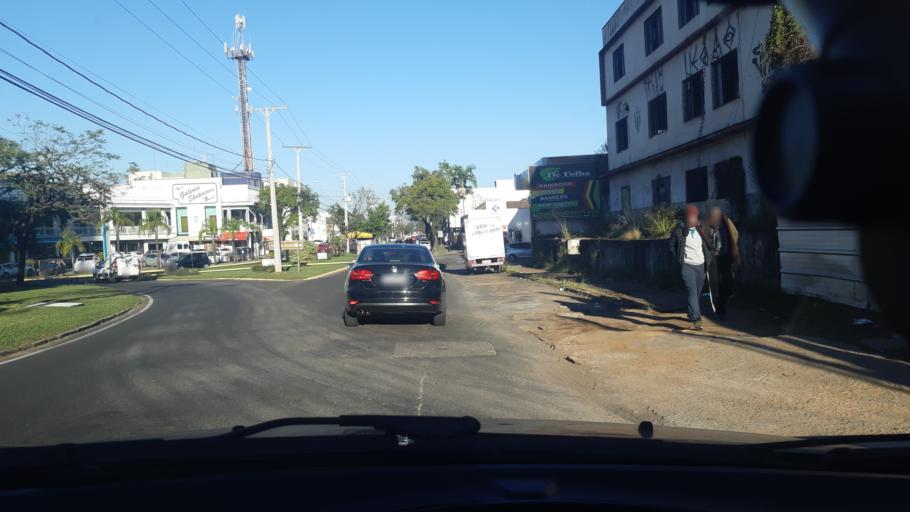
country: BR
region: Rio Grande do Sul
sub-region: Sao Leopoldo
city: Sao Leopoldo
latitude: -29.7701
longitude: -51.1353
